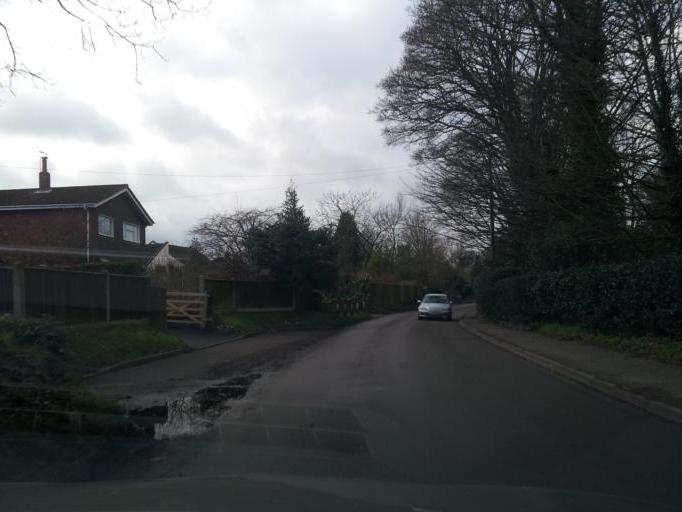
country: GB
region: England
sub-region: Norfolk
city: Lingwood
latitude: 52.6174
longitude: 1.4724
